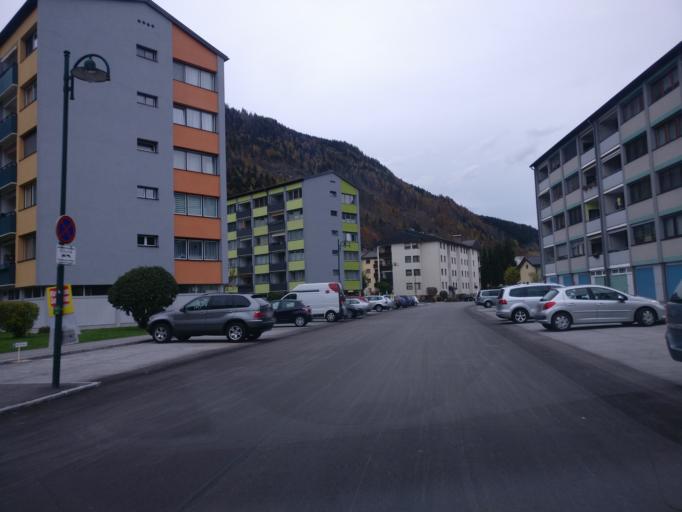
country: AT
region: Salzburg
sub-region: Politischer Bezirk Sankt Johann im Pongau
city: Bischofshofen
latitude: 47.4282
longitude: 13.2159
